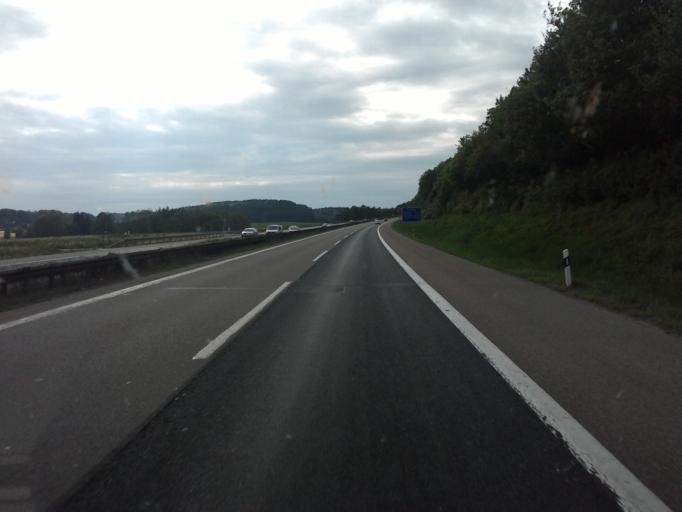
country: DE
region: Bavaria
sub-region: Upper Palatinate
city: Deining
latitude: 49.2841
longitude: 11.5701
